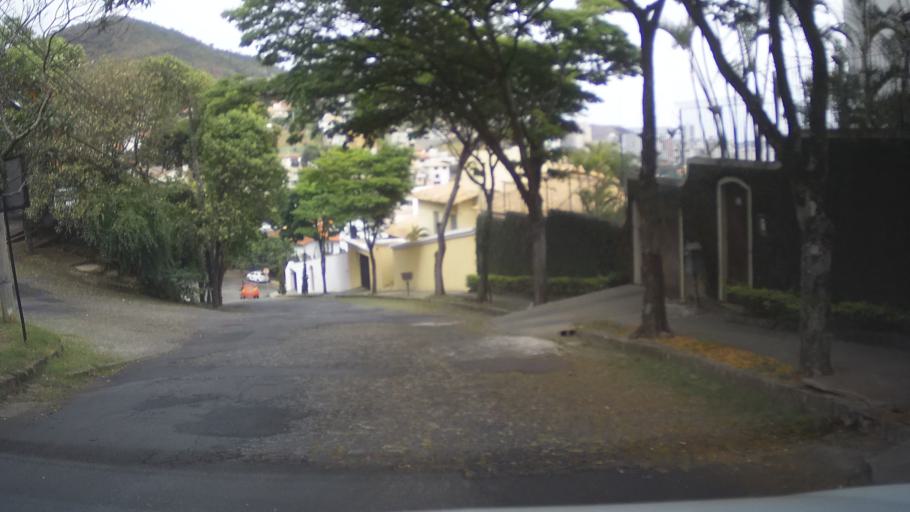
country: BR
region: Minas Gerais
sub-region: Belo Horizonte
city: Belo Horizonte
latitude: -19.9520
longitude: -43.9196
